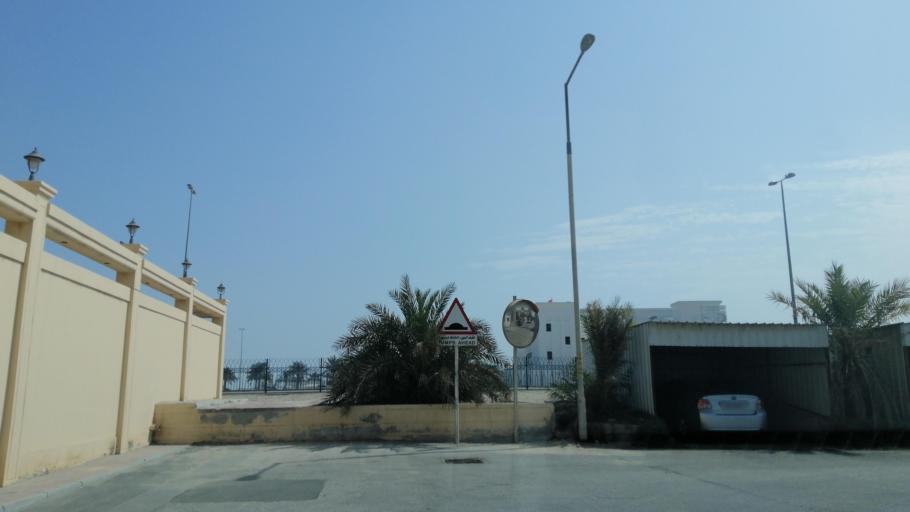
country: BH
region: Muharraq
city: Al Hadd
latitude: 26.2497
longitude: 50.6571
